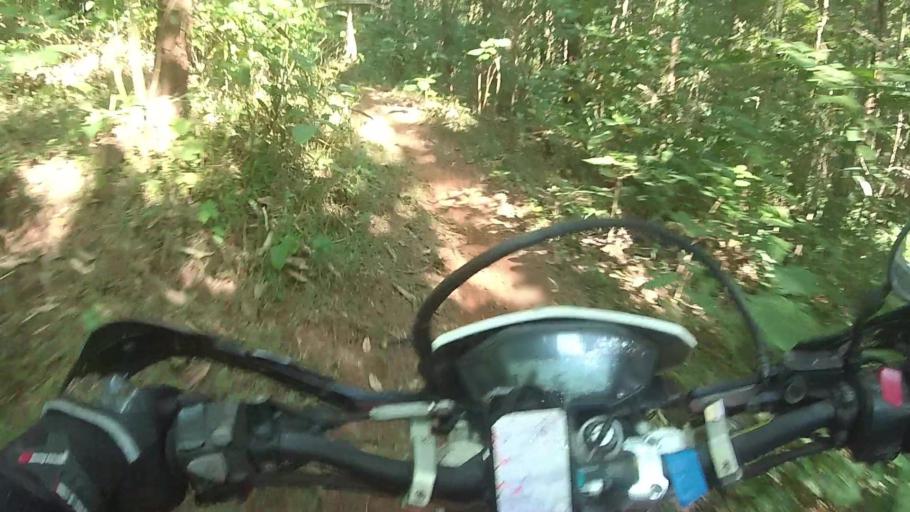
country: TH
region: Chiang Mai
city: Samoeng
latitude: 18.9728
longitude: 98.8188
